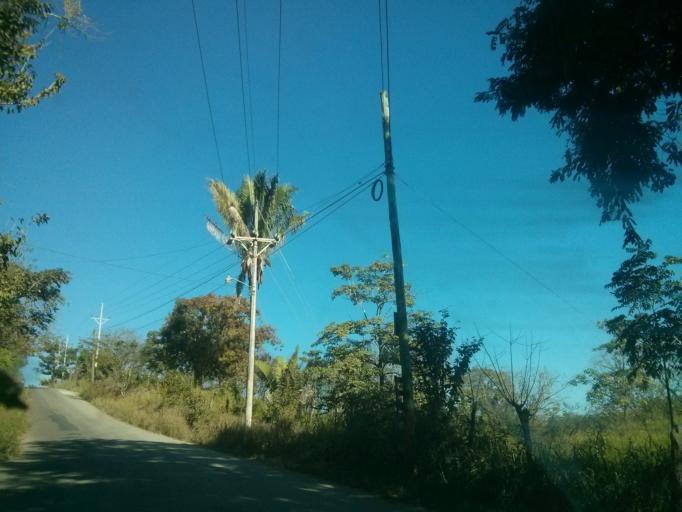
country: CR
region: Puntarenas
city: Paquera
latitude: 9.6747
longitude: -85.1148
